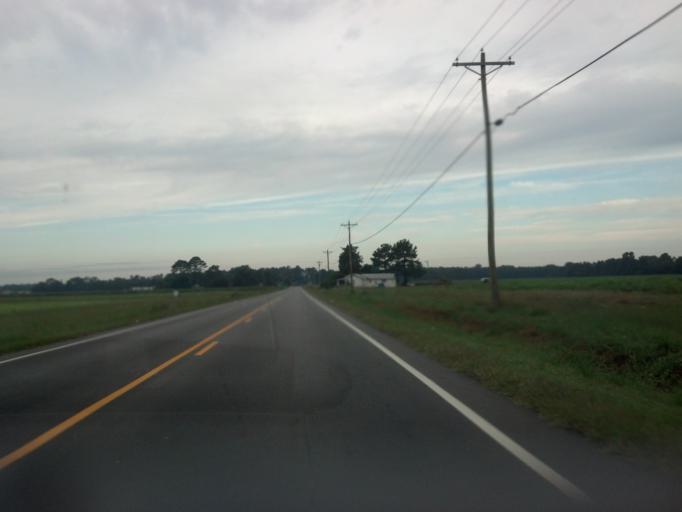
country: US
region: North Carolina
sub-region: Greene County
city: Maury
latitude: 35.4623
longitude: -77.5098
